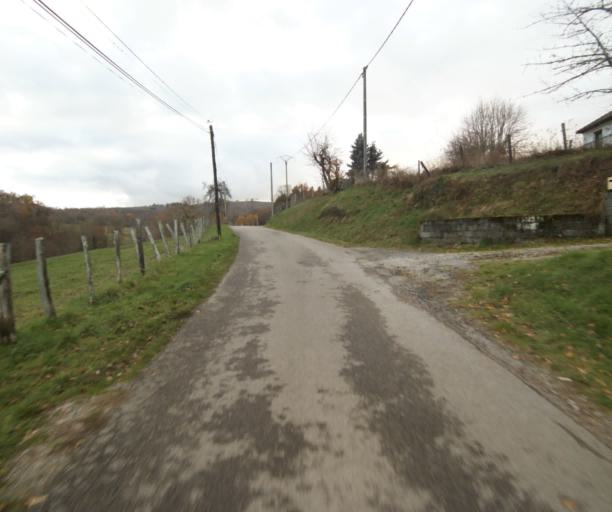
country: FR
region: Limousin
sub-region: Departement de la Correze
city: Sainte-Fortunade
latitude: 45.2209
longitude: 1.7838
